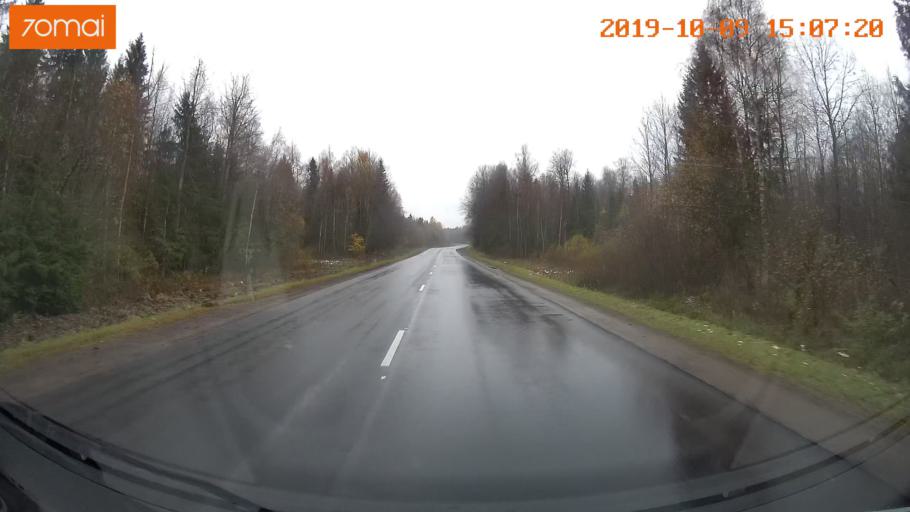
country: RU
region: Kostroma
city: Susanino
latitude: 58.2205
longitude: 41.6512
